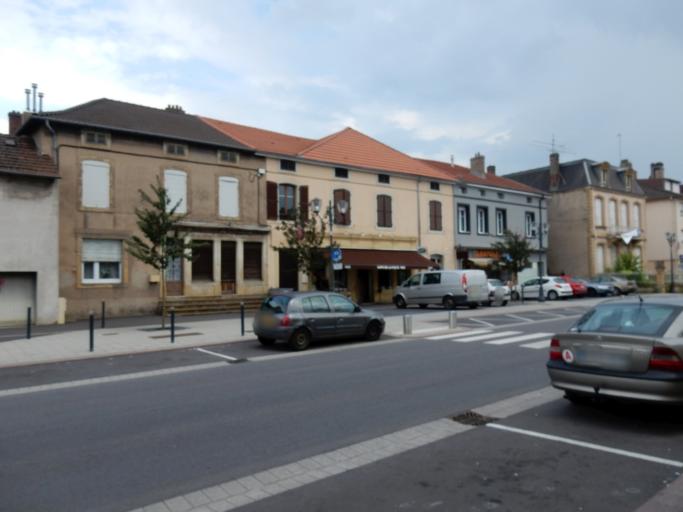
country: FR
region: Lorraine
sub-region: Departement de la Moselle
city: Uckange
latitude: 49.3017
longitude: 6.1577
